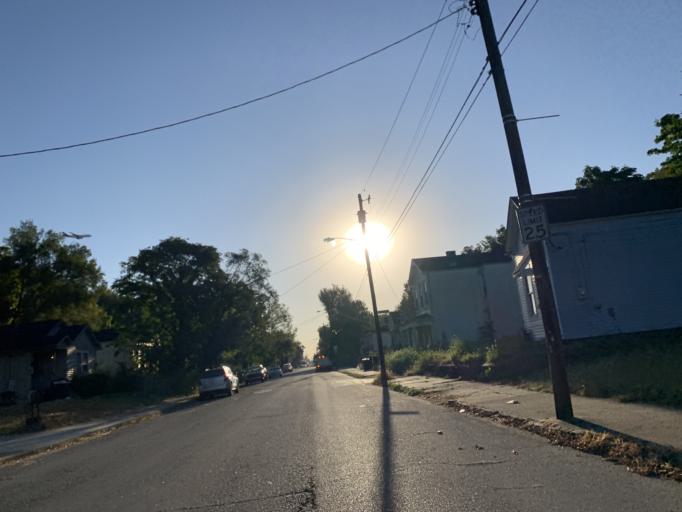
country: US
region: Kentucky
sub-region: Jefferson County
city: Louisville
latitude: 38.2420
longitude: -85.7845
